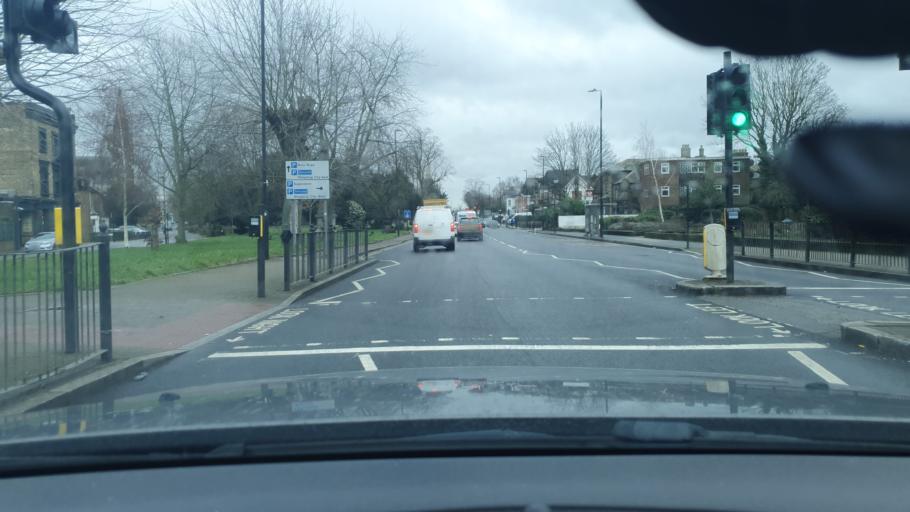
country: GB
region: England
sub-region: Greater London
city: Wood Green
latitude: 51.6011
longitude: -0.1171
